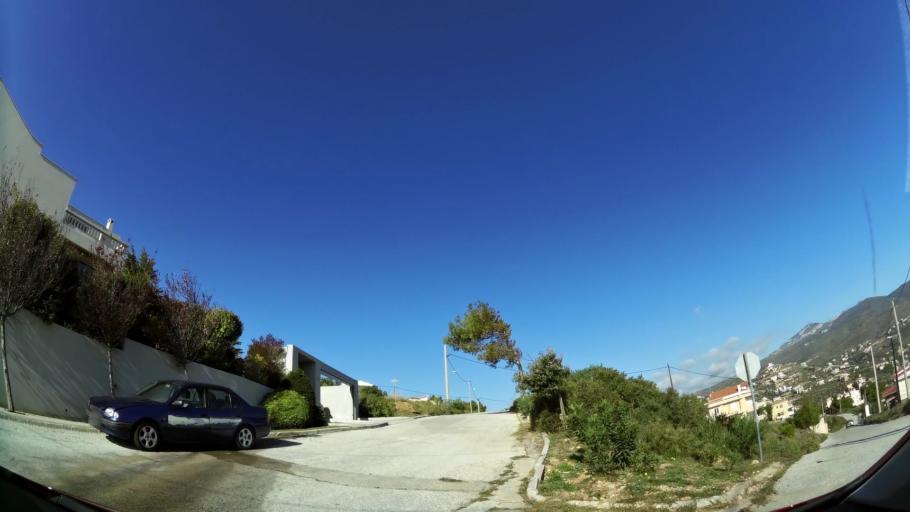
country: GR
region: Attica
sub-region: Nomarchia Anatolikis Attikis
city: Dhrafi
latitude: 38.0252
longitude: 23.9018
